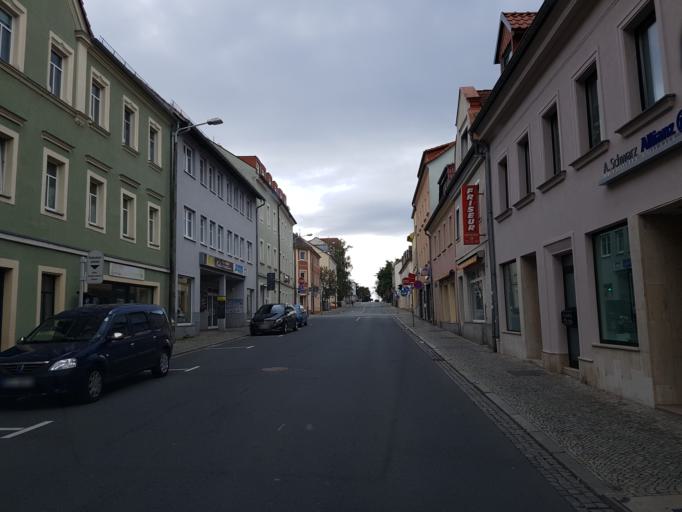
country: DE
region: Saxony
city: Riesa
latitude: 51.3038
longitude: 13.3061
